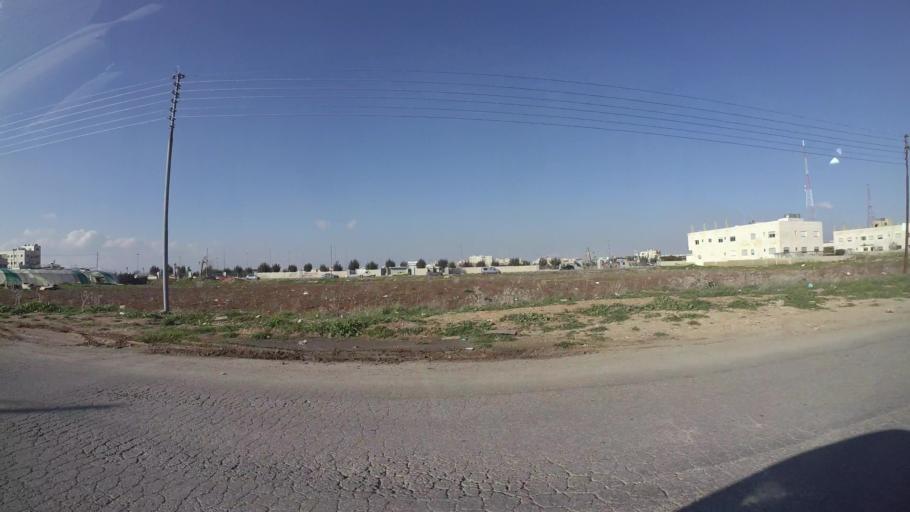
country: JO
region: Amman
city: Al Quwaysimah
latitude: 31.9020
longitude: 35.9260
